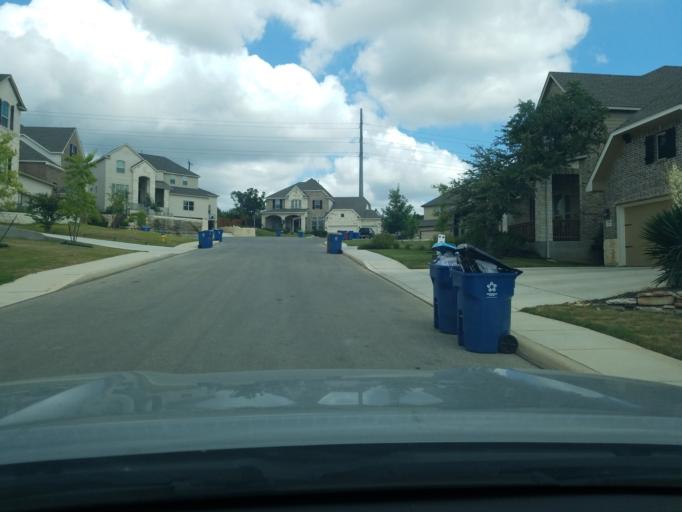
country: US
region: Texas
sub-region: Bexar County
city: Timberwood Park
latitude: 29.6667
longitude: -98.5110
